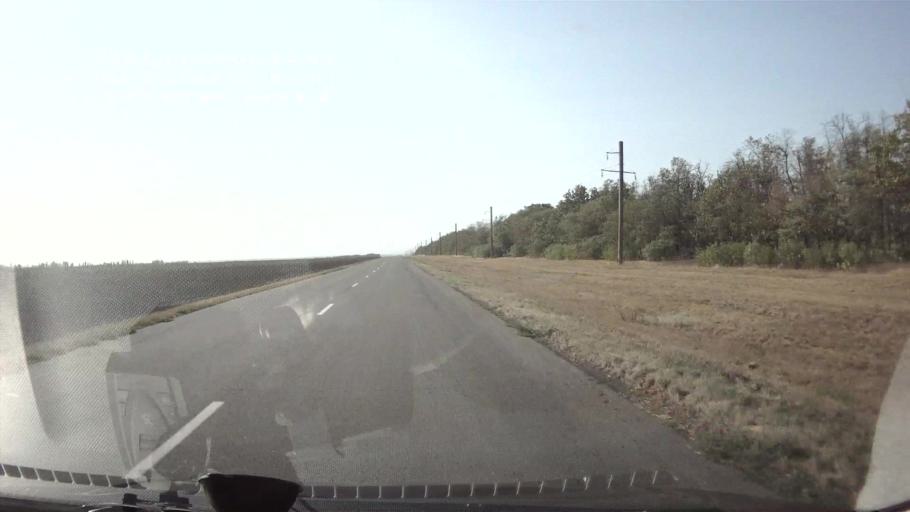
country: RU
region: Rostov
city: Tselina
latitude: 46.5132
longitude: 40.8995
